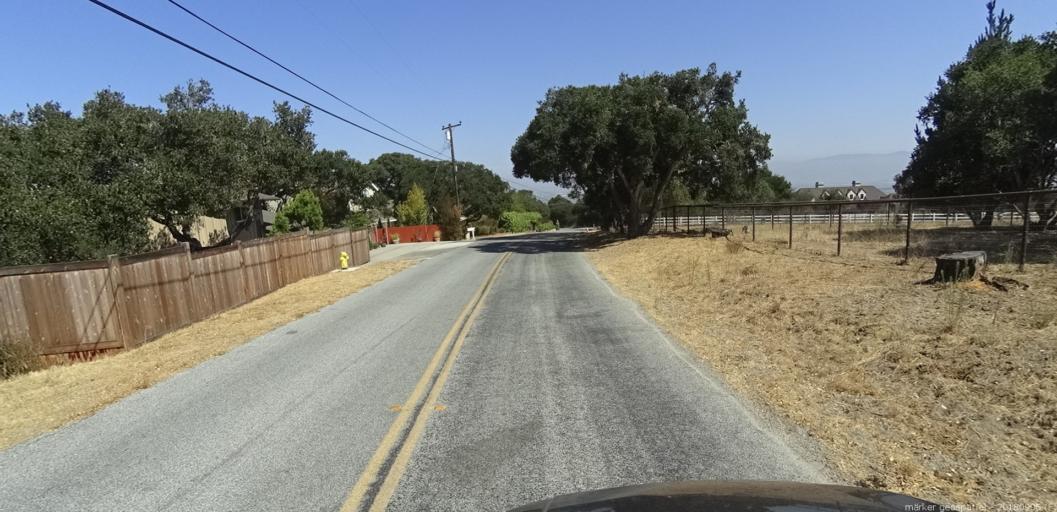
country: US
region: California
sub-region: Monterey County
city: Salinas
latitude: 36.5796
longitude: -121.6310
